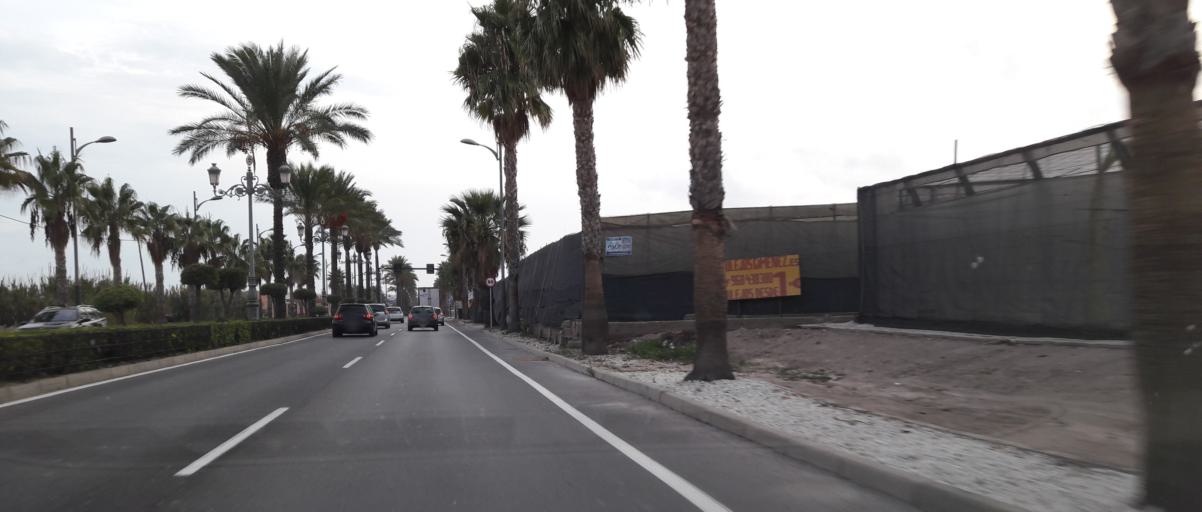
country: ES
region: Andalusia
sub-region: Provincia de Almeria
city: Roquetas de Mar
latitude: 36.7959
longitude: -2.6029
